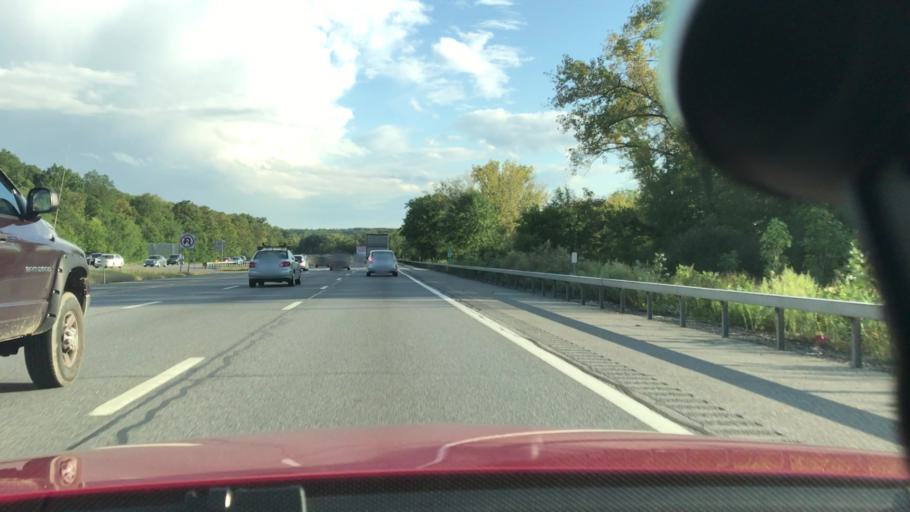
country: US
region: New York
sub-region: Albany County
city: Cohoes
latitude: 42.7996
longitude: -73.7651
